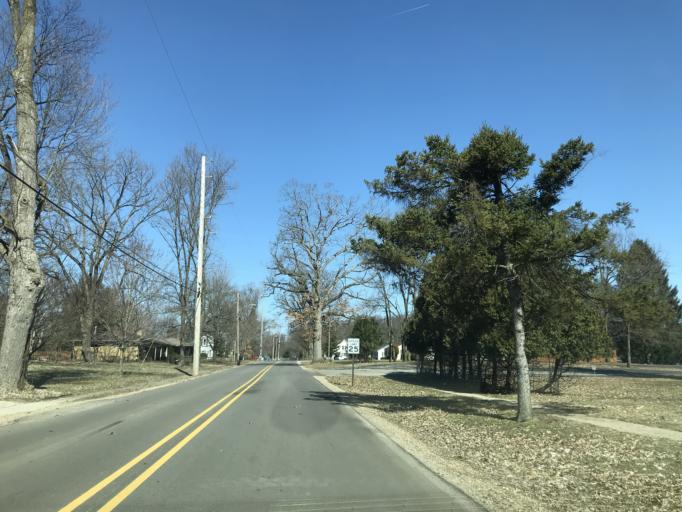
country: US
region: Michigan
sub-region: Hillsdale County
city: Jonesville
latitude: 41.9810
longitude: -84.6695
